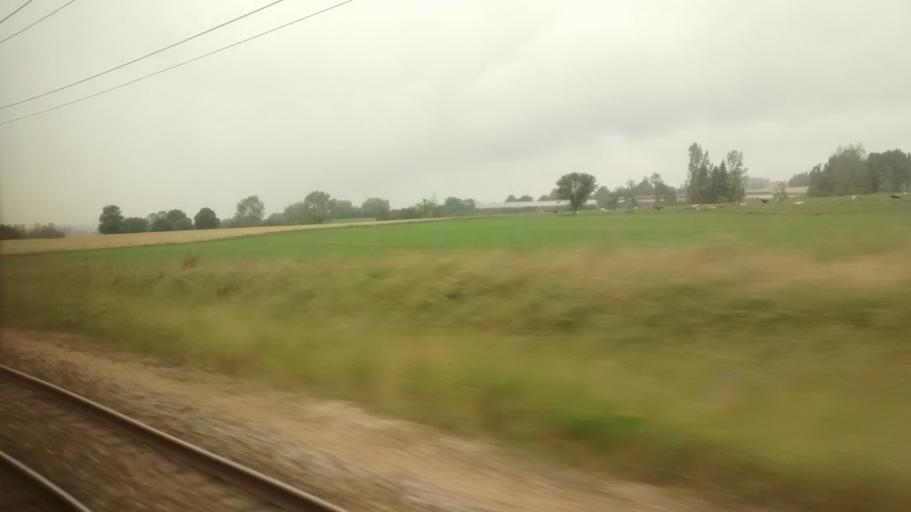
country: FR
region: Pays de la Loire
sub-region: Departement de la Sarthe
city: Vibraye
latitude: 48.0824
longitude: 0.8109
